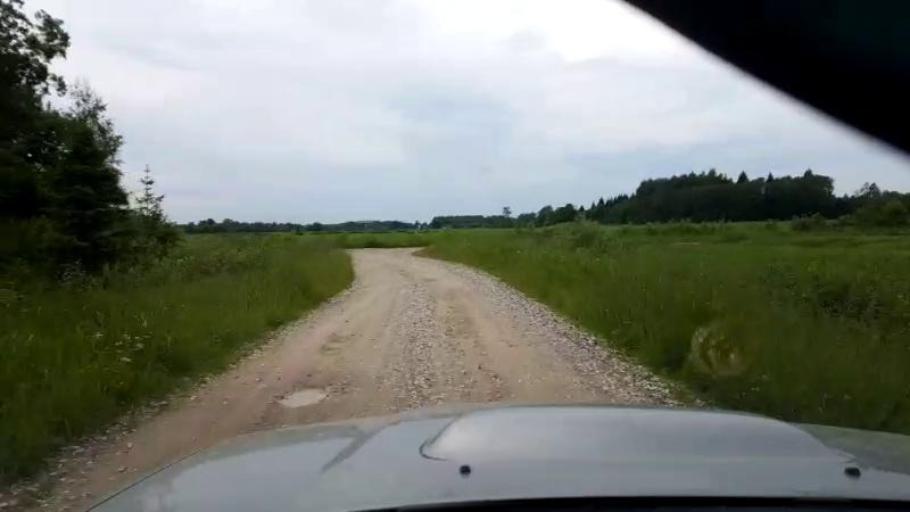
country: EE
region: Paernumaa
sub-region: Tootsi vald
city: Tootsi
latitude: 58.5423
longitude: 24.7353
